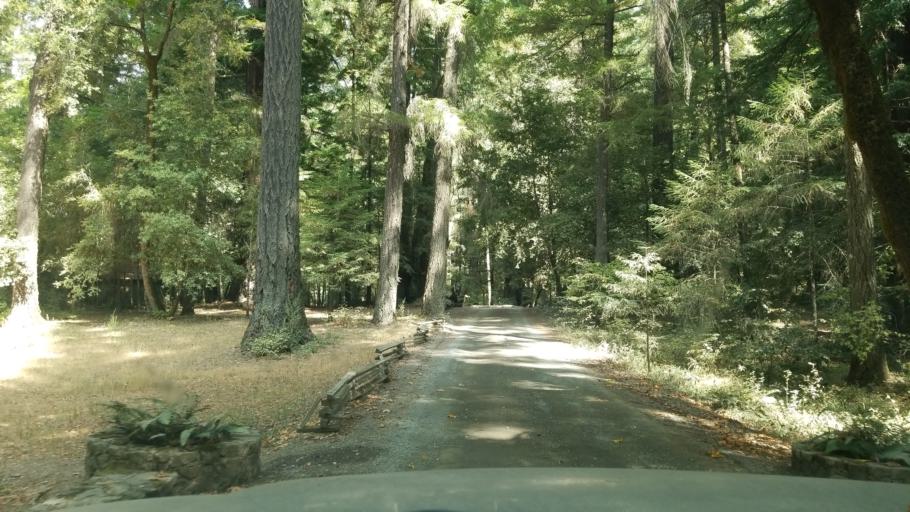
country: US
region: California
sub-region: Humboldt County
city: Redway
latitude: 39.8593
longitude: -123.7181
